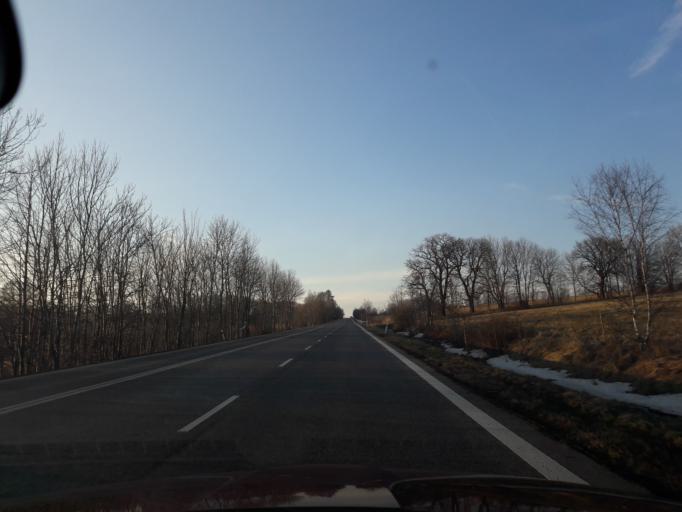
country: CZ
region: Ustecky
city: Dolni Podluzi
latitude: 50.8907
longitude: 14.5749
